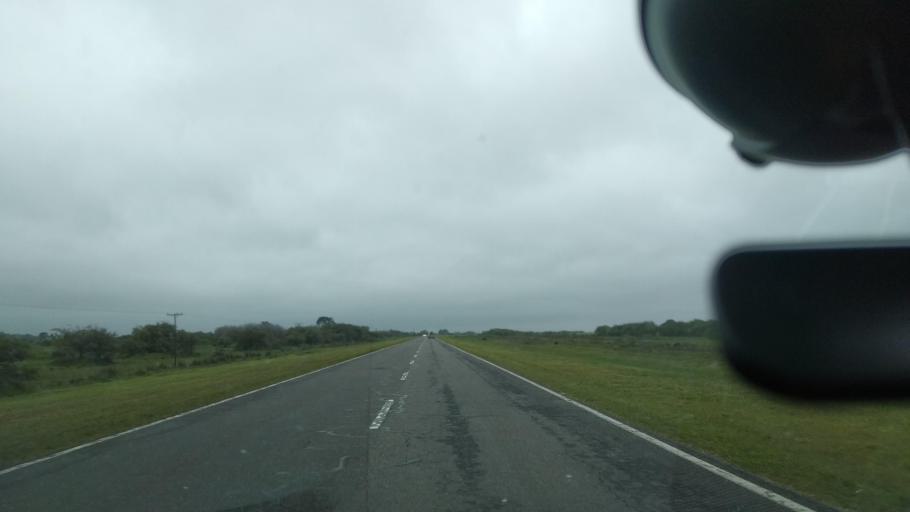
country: AR
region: Buenos Aires
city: Veronica
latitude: -35.6389
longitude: -57.3108
